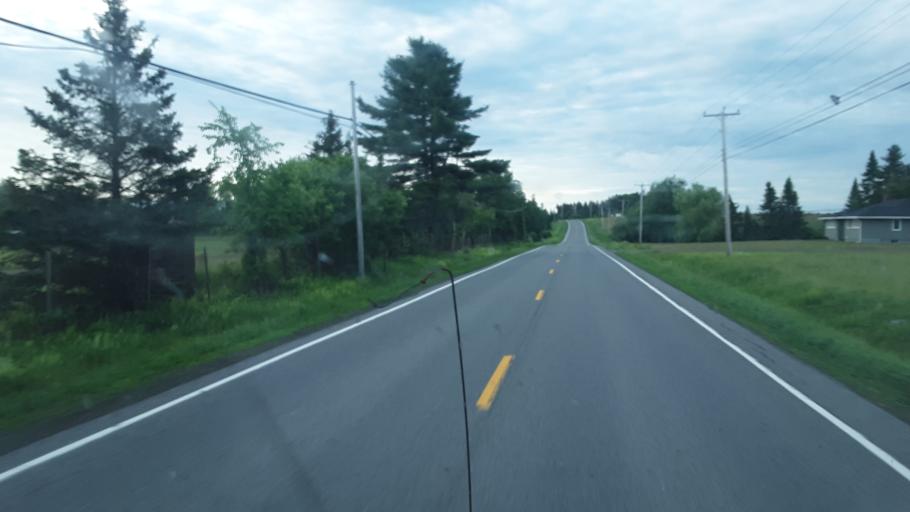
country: US
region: Maine
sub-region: Aroostook County
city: Presque Isle
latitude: 46.6142
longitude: -68.3995
